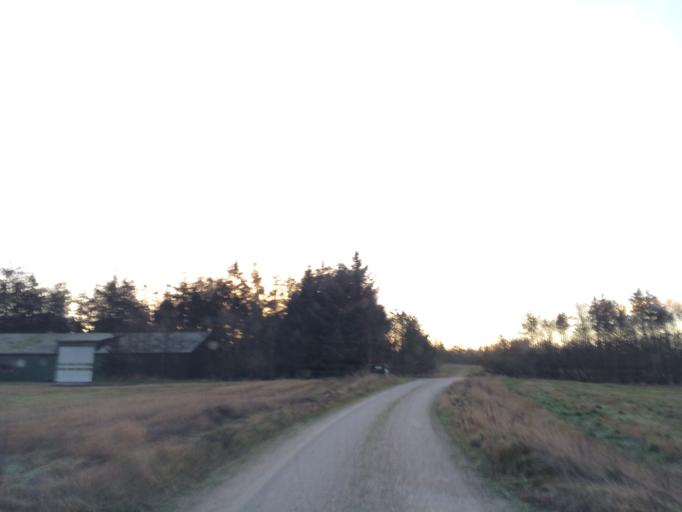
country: DK
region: Central Jutland
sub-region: Holstebro Kommune
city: Ulfborg
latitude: 56.2275
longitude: 8.4936
